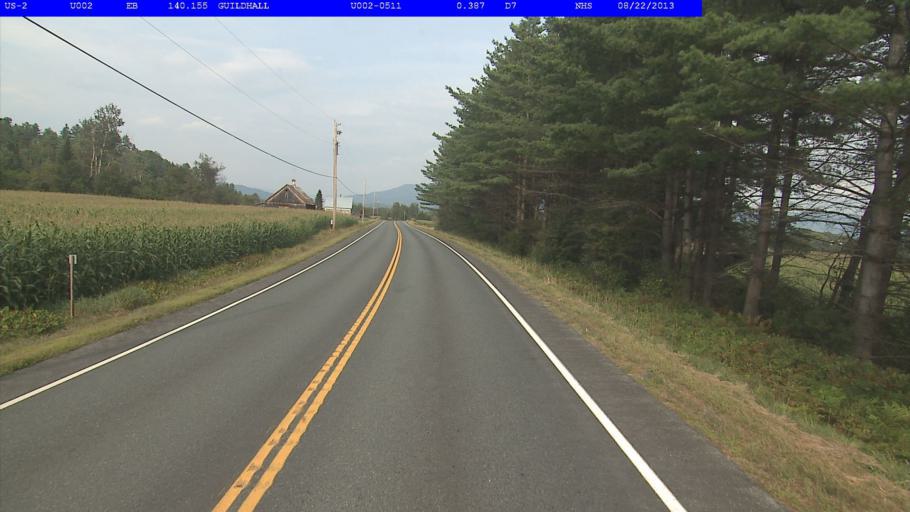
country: US
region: New Hampshire
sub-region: Coos County
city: Lancaster
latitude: 44.4878
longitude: -71.6038
